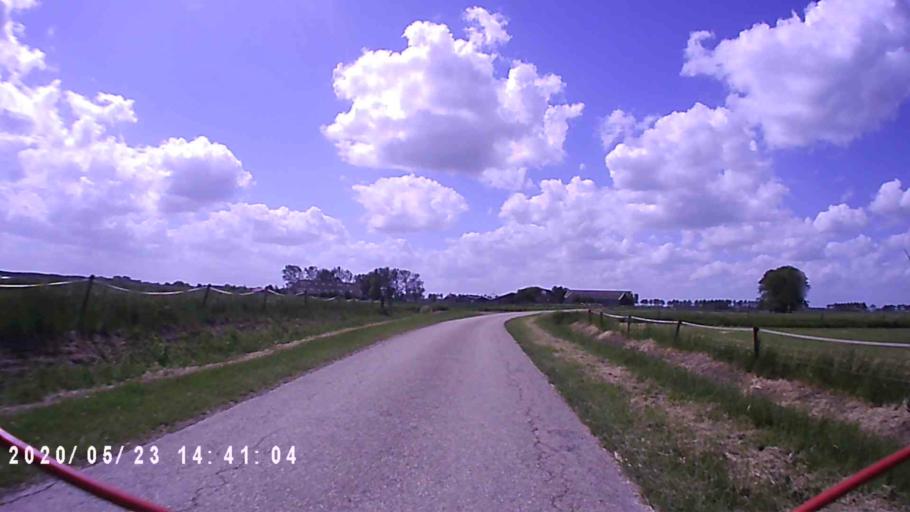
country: NL
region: Groningen
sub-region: Gemeente Delfzijl
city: Delfzijl
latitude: 53.2722
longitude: 6.9672
